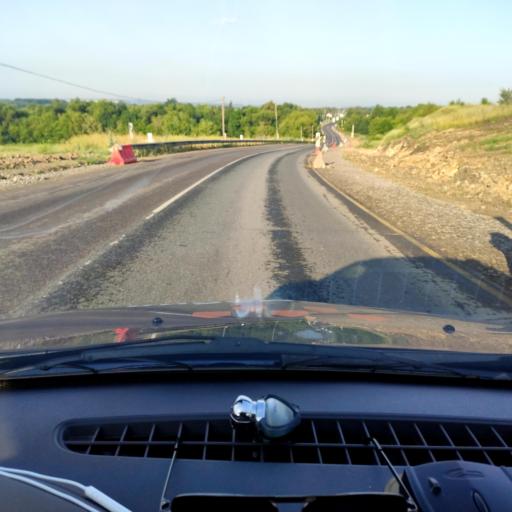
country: RU
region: Lipetsk
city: Kazaki
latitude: 52.5029
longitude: 38.0851
